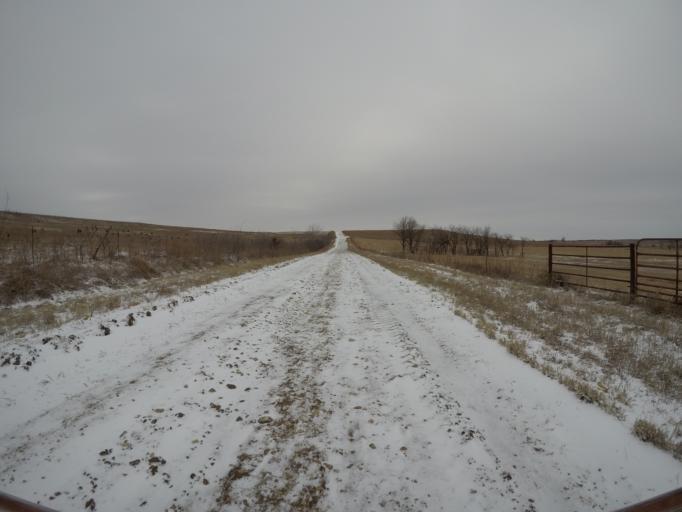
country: US
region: Kansas
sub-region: Wabaunsee County
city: Alma
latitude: 38.8679
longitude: -96.1135
